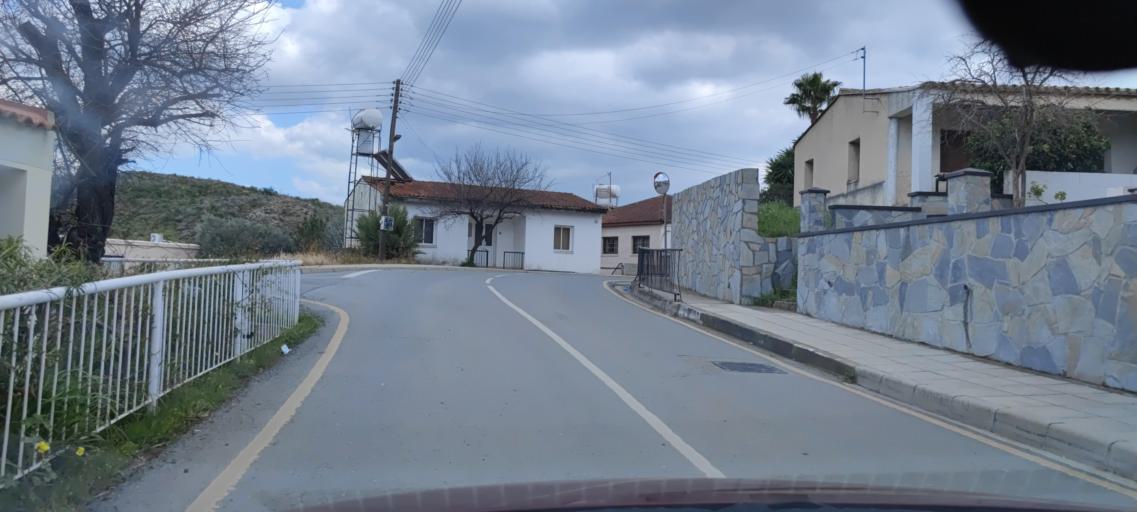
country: CY
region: Larnaka
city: Kornos
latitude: 34.9202
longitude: 33.3986
